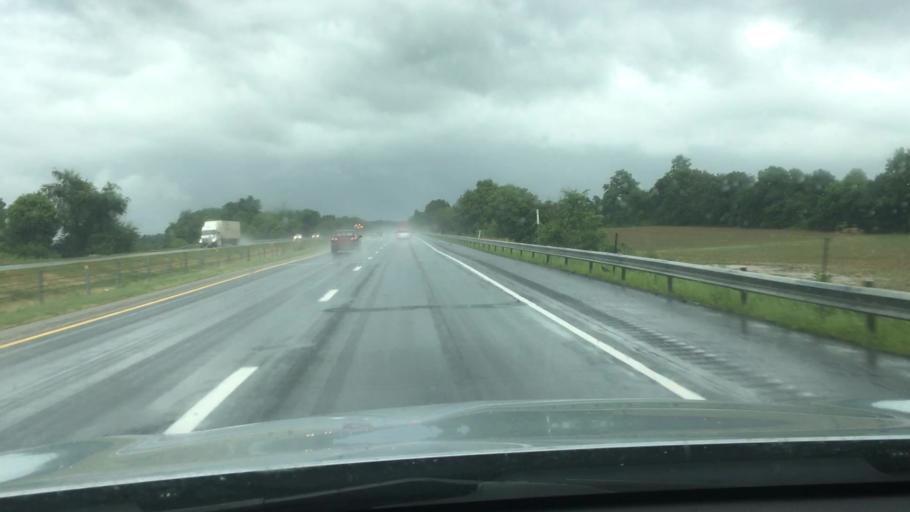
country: US
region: Pennsylvania
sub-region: Cumberland County
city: Shippensburg
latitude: 40.0680
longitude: -77.4670
